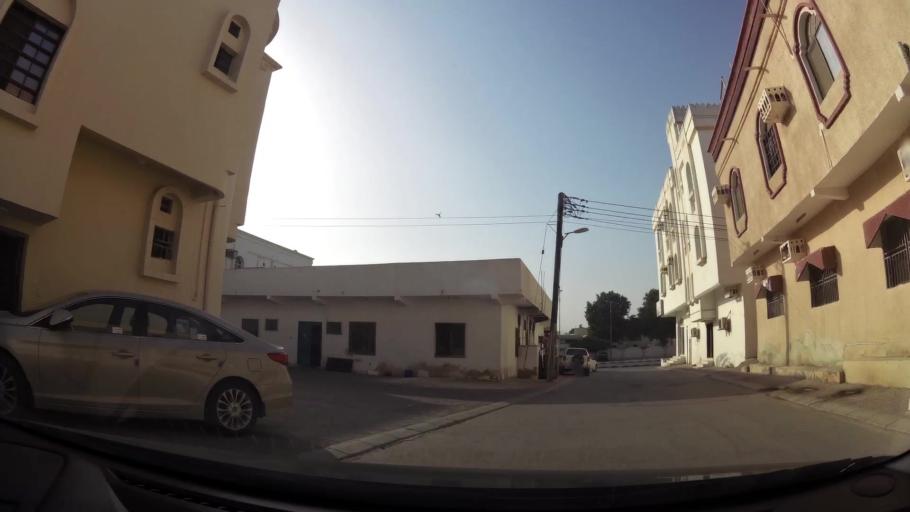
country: OM
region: Zufar
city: Salalah
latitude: 17.0104
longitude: 54.0787
